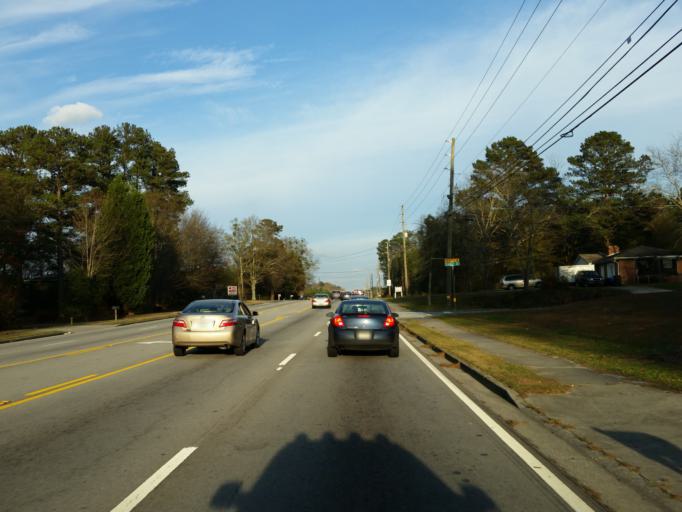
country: US
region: Georgia
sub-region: Cobb County
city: Powder Springs
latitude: 33.8635
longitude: -84.6384
